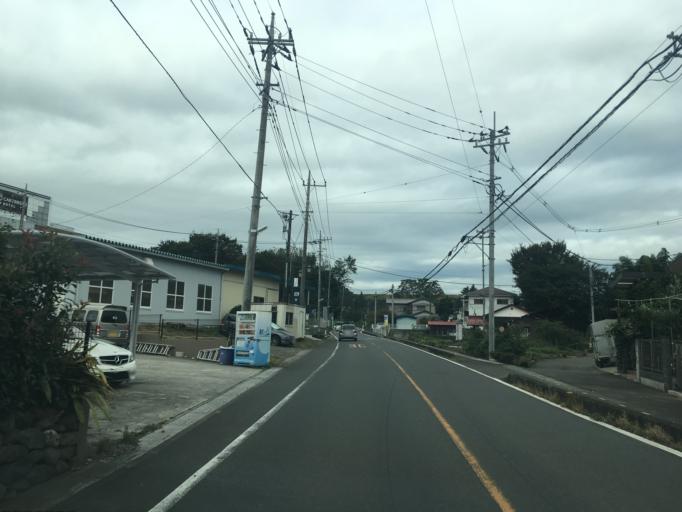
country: JP
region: Tokyo
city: Higashimurayama-shi
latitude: 35.7756
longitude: 139.4204
